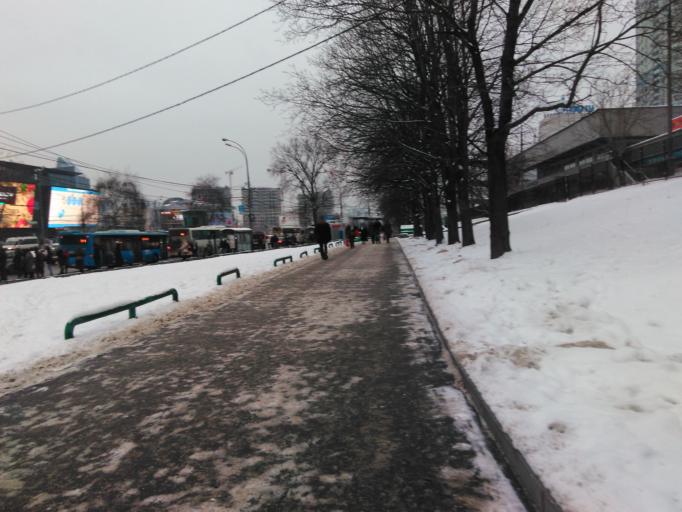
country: RU
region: Moscow
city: Troparevo
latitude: 55.6614
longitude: 37.4829
